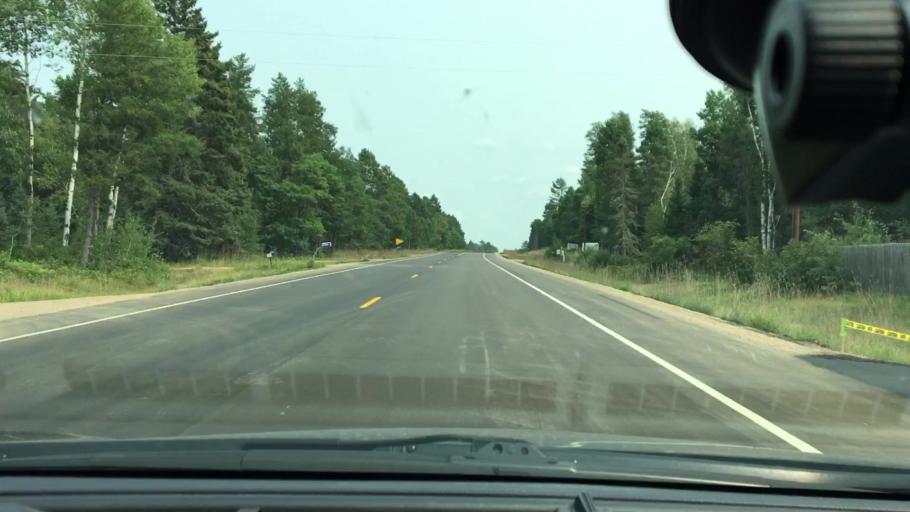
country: US
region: Minnesota
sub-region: Crow Wing County
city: Nisswa
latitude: 46.5291
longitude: -94.2589
